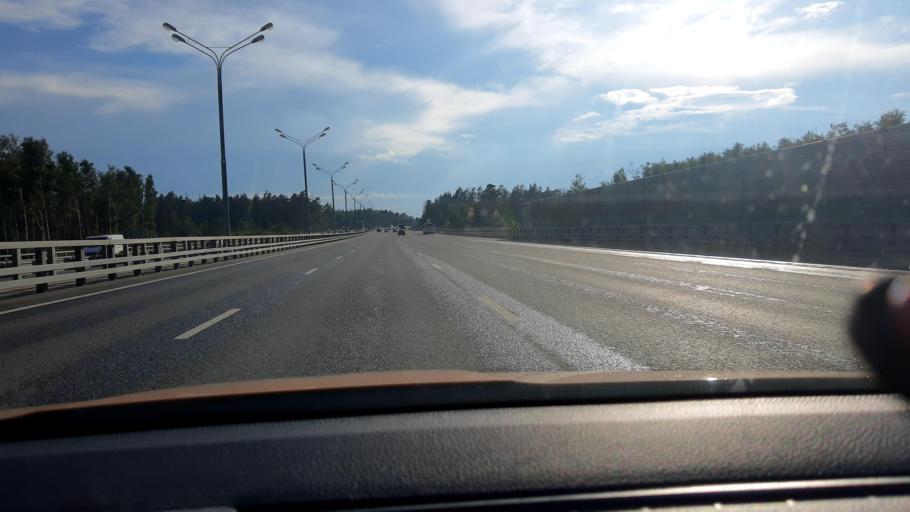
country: RU
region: Moskovskaya
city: Zhavoronki
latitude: 55.6138
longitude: 37.0795
